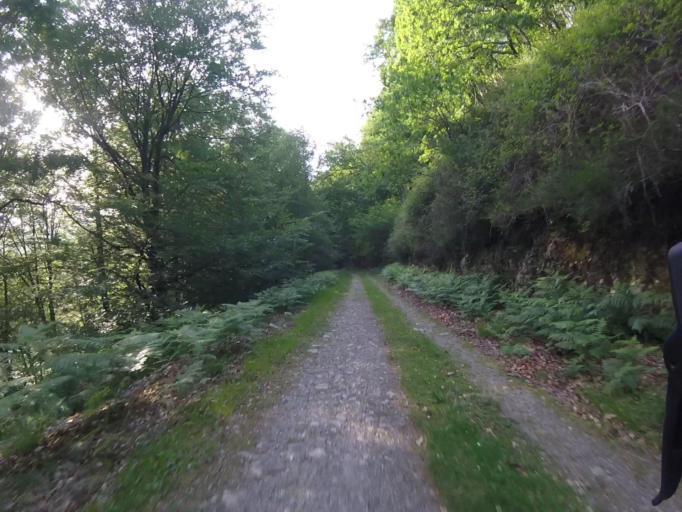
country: ES
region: Navarre
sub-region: Provincia de Navarra
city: Arano
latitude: 43.2325
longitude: -1.8750
